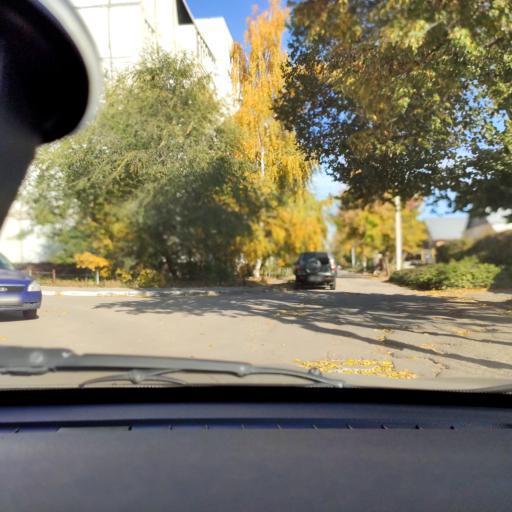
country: RU
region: Samara
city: Tol'yatti
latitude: 53.5239
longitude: 49.3979
